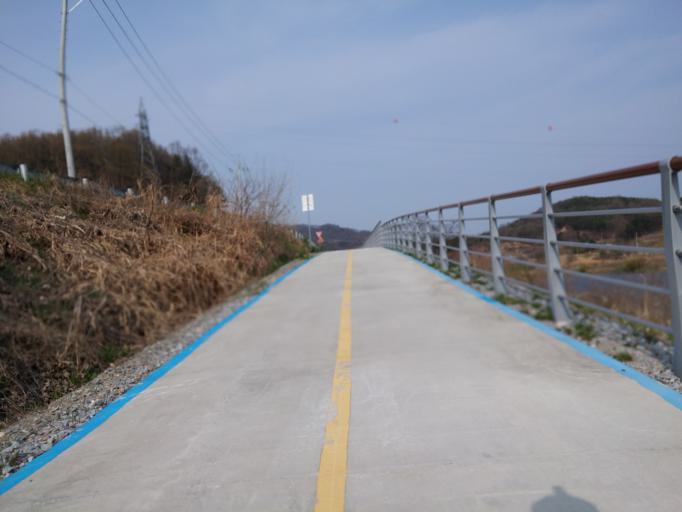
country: KR
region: Daejeon
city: Songgang-dong
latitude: 36.4936
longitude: 127.3733
